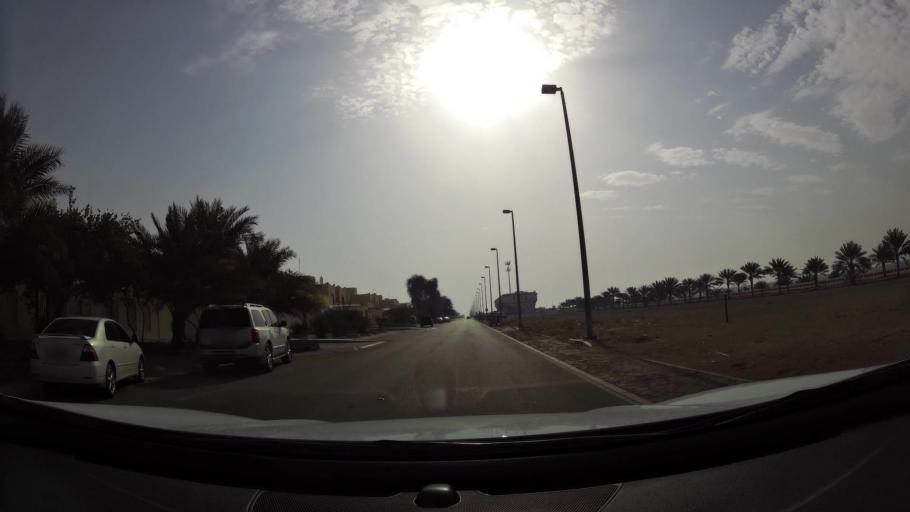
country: AE
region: Abu Dhabi
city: Abu Dhabi
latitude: 24.2409
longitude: 54.7153
